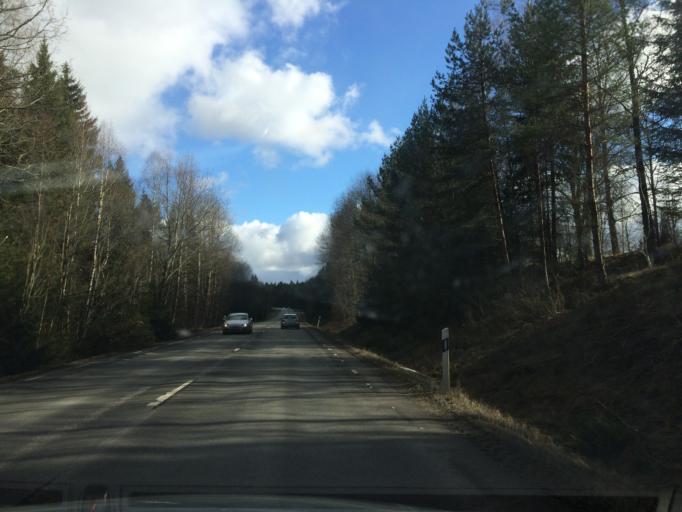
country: SE
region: Vaestra Goetaland
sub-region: Skara Kommun
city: Skara
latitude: 58.3152
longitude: 13.4411
